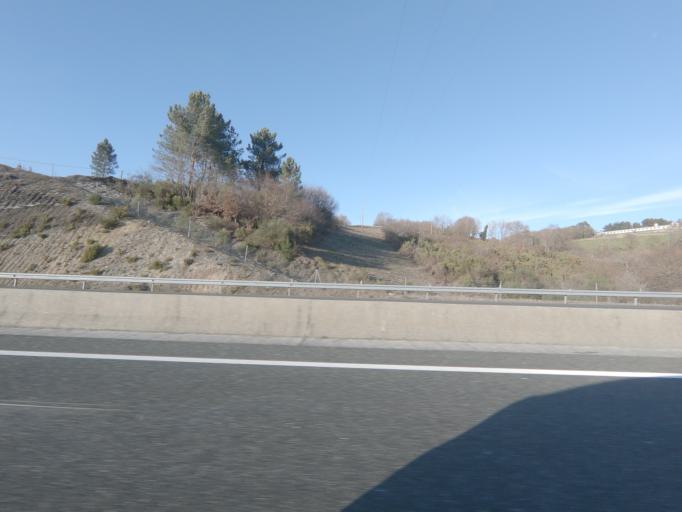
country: ES
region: Galicia
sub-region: Provincia de Pontevedra
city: Dozon
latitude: 42.5877
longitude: -8.0775
